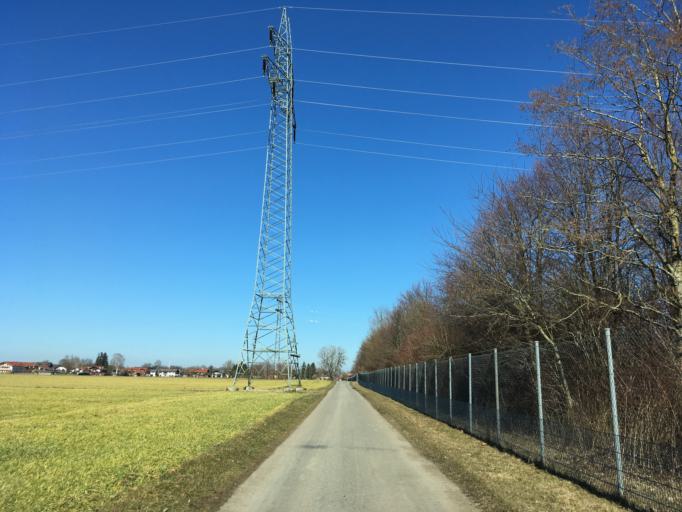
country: DE
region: Bavaria
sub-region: Upper Bavaria
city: Bad Aibling
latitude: 47.8472
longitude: 11.9883
